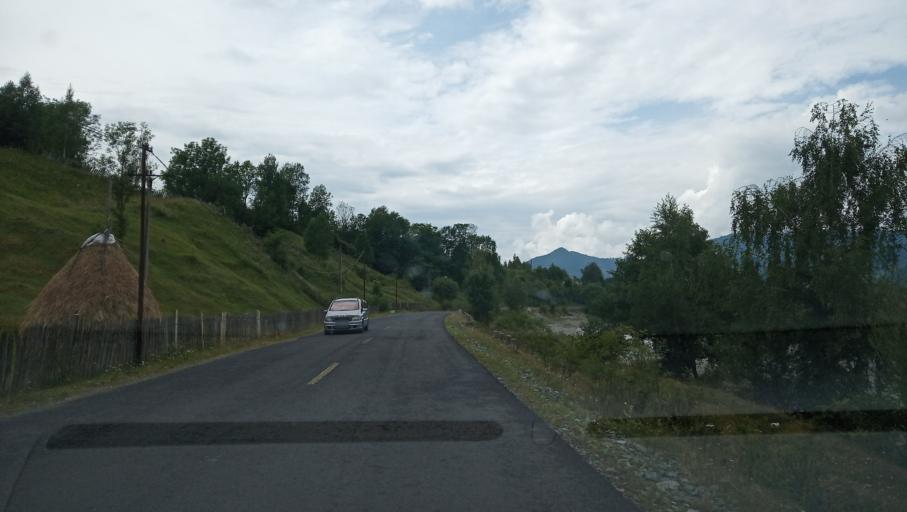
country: RO
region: Hunedoara
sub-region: Oras Petrila
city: Petrila
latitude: 45.4186
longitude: 23.4290
